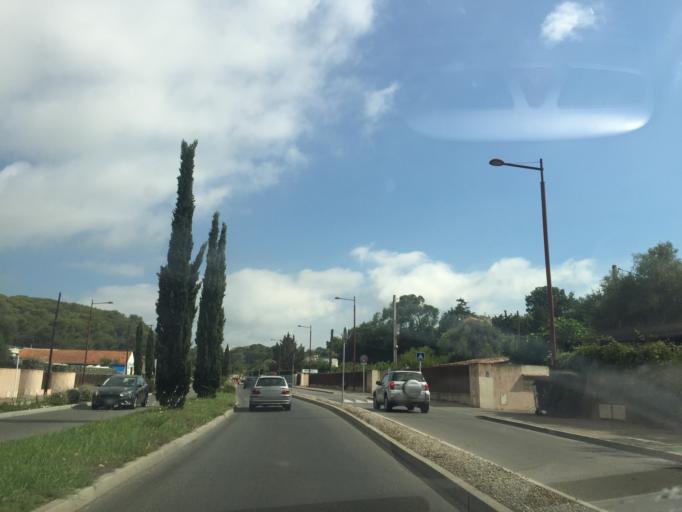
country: FR
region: Provence-Alpes-Cote d'Azur
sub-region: Departement des Alpes-Maritimes
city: Vallauris
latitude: 43.5825
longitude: 7.0897
